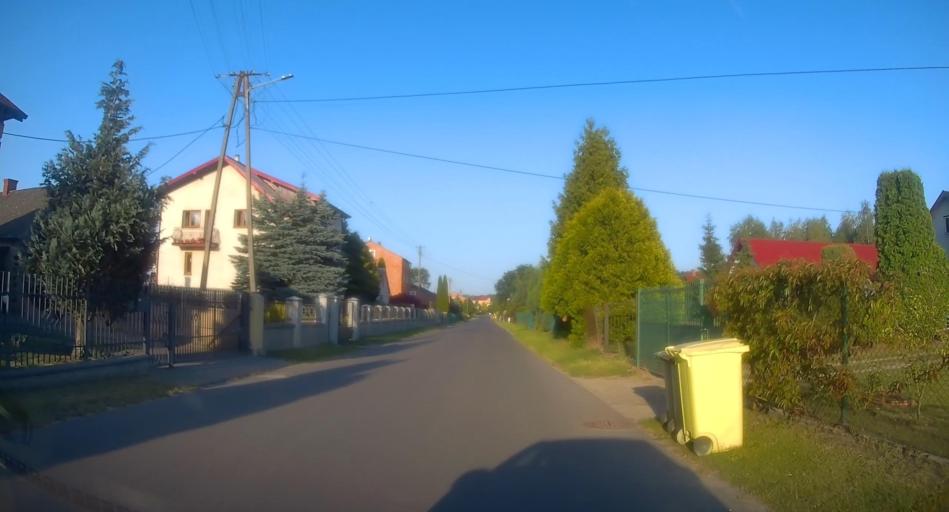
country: PL
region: Lodz Voivodeship
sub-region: Powiat skierniewicki
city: Kaweczyn Nowy
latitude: 51.8817
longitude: 20.2752
